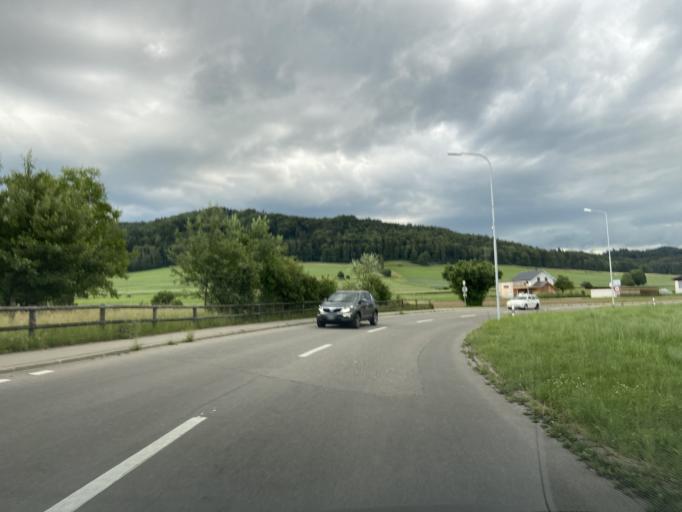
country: CH
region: Thurgau
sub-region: Muenchwilen District
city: Aadorf
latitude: 47.4796
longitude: 8.9054
